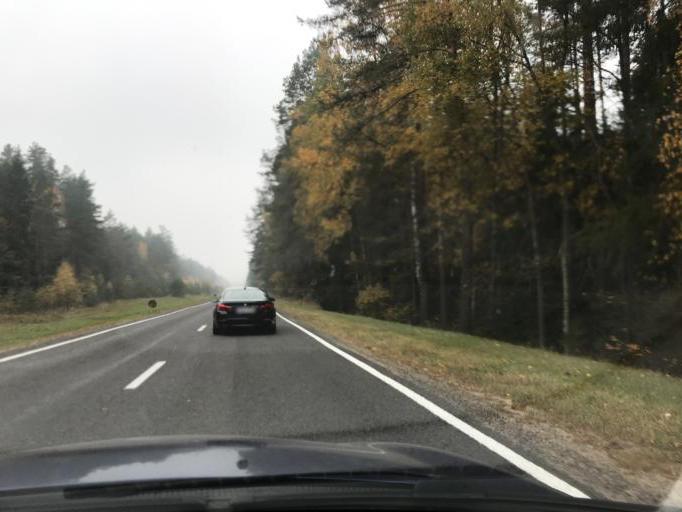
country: LT
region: Alytaus apskritis
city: Druskininkai
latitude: 53.8849
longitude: 23.9068
